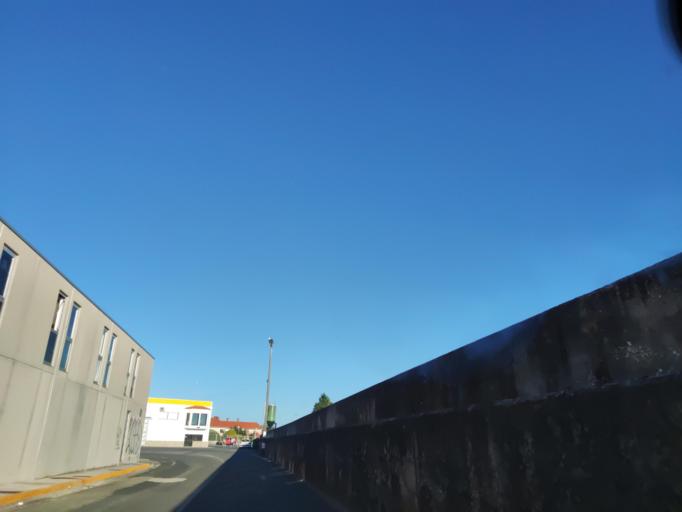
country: ES
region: Galicia
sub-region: Provincia da Coruna
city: Boiro
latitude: 42.6128
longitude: -8.8891
